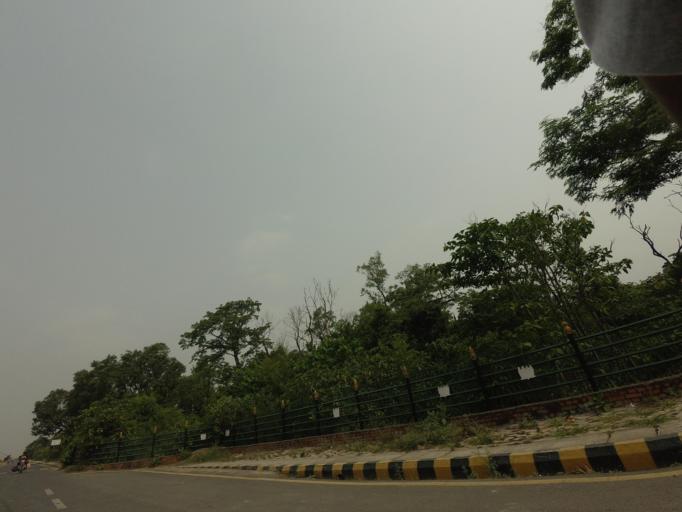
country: IN
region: Uttar Pradesh
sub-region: Maharajganj
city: Nautanwa
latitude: 27.4624
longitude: 83.2814
